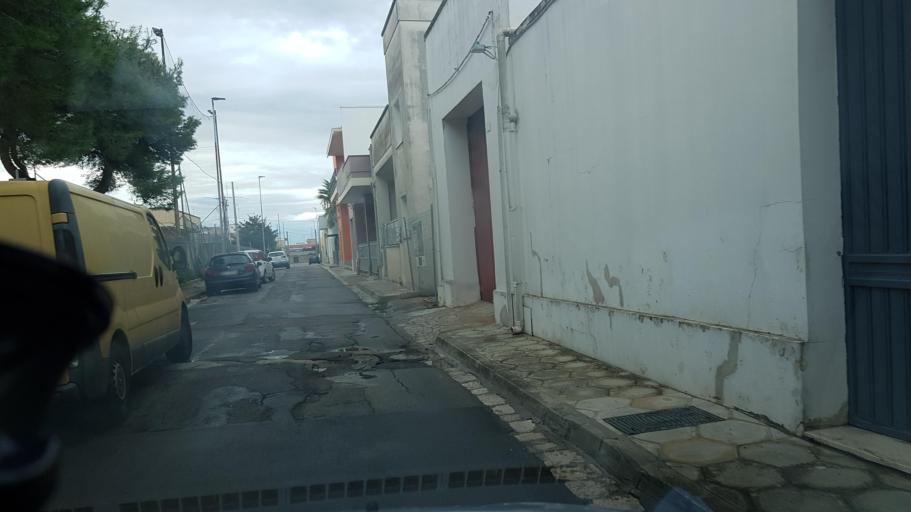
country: IT
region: Apulia
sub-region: Provincia di Lecce
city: Carmiano
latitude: 40.3480
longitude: 18.0388
